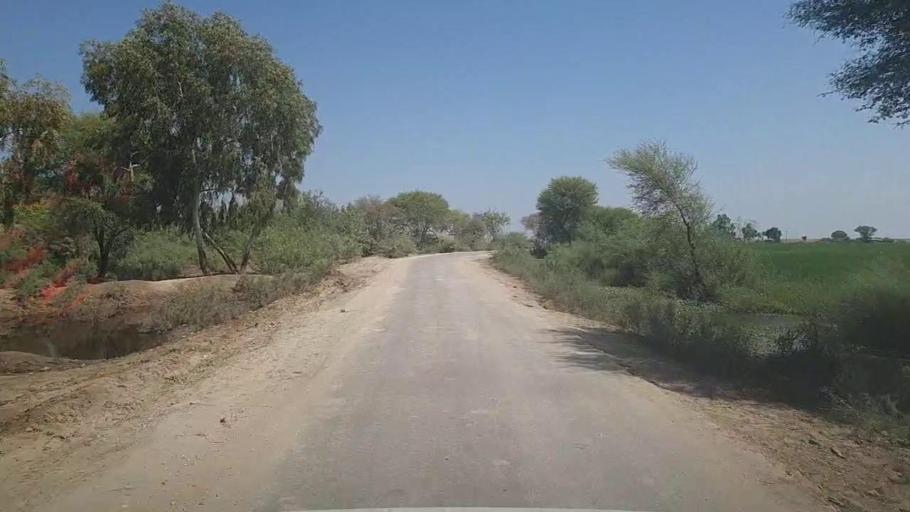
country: PK
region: Sindh
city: Kashmor
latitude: 28.2843
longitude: 69.4375
